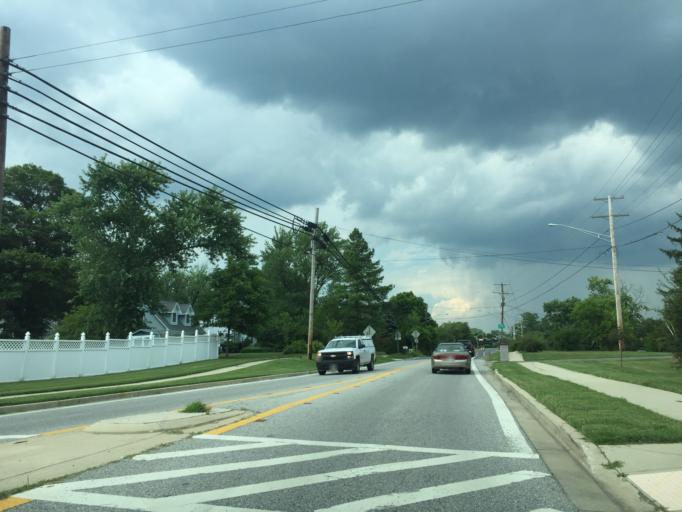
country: US
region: Maryland
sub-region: Montgomery County
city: Burtonsville
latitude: 39.0960
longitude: -76.9458
